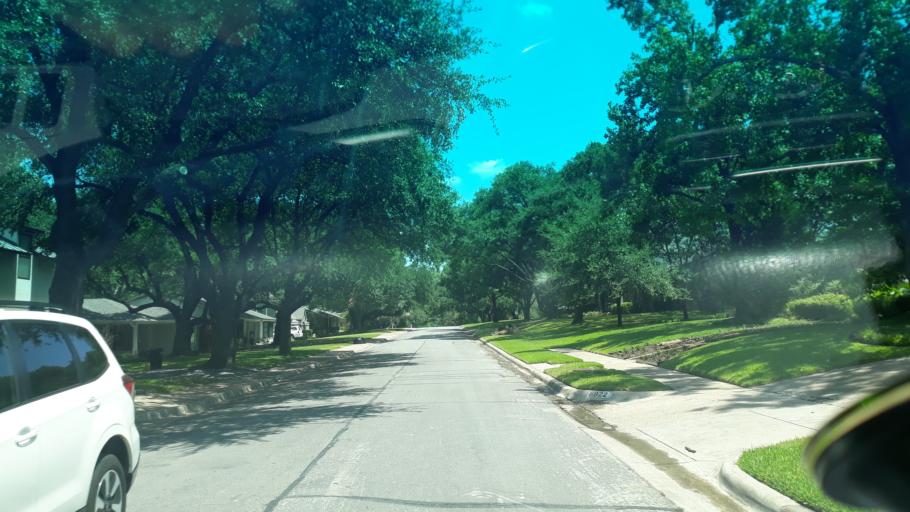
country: US
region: Texas
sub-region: Dallas County
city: Highland Park
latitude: 32.8244
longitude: -96.7404
